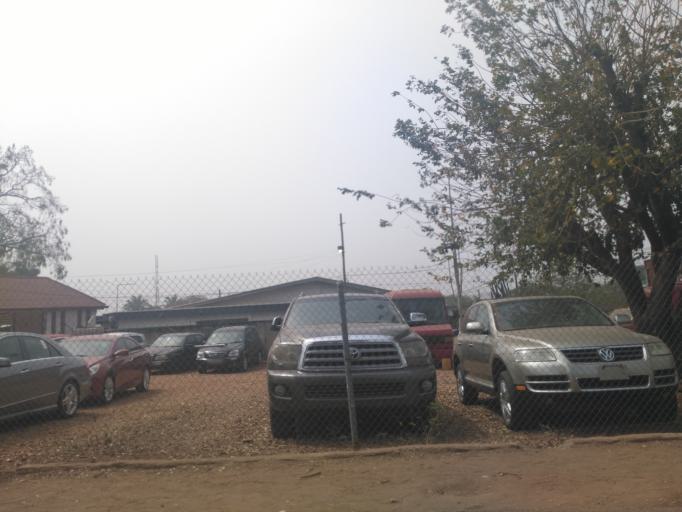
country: GH
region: Ashanti
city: Kumasi
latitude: 6.6936
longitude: -1.6353
